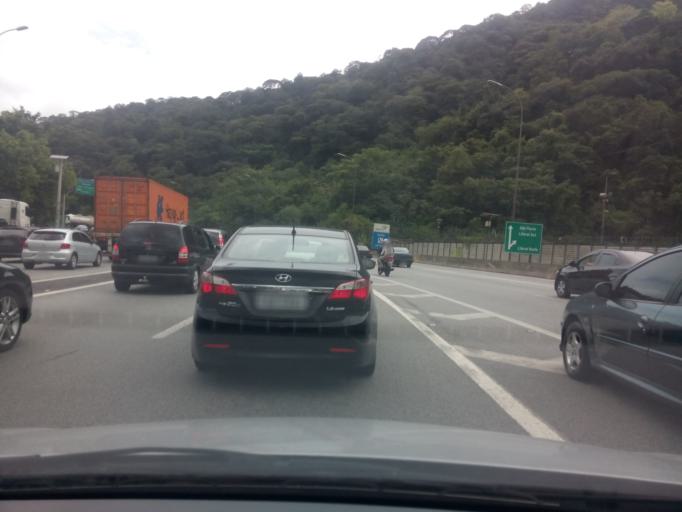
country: BR
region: Sao Paulo
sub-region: Cubatao
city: Cubatao
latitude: -23.8913
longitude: -46.4414
